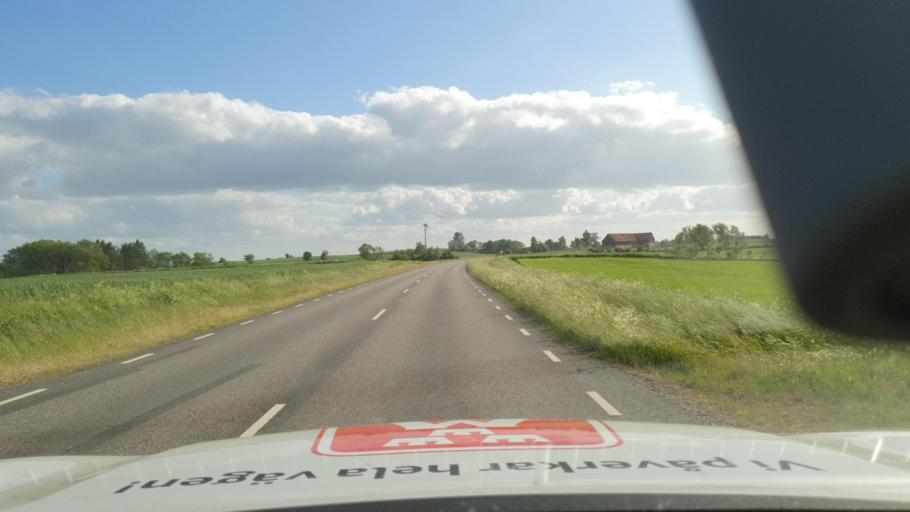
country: SE
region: Skane
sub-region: Tomelilla Kommun
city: Tomelilla
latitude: 55.5748
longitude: 13.9998
